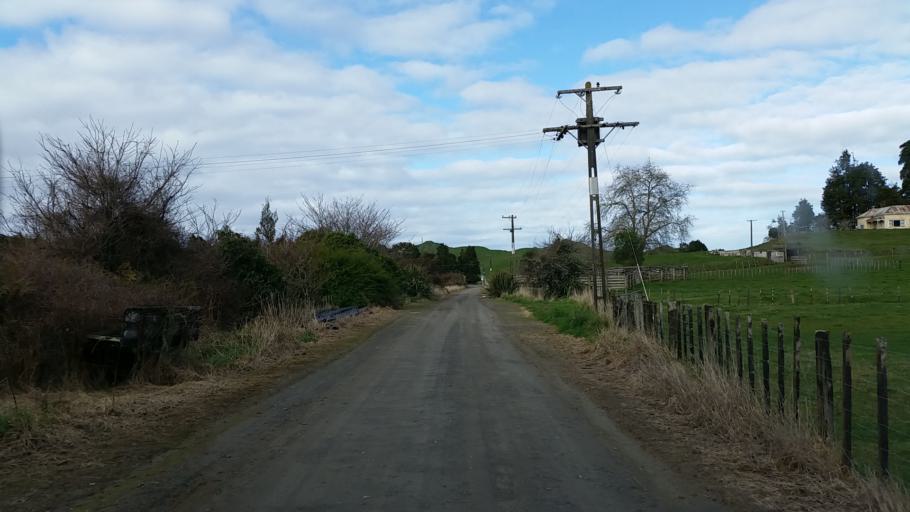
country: NZ
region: Taranaki
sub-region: South Taranaki District
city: Eltham
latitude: -39.2322
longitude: 174.5198
